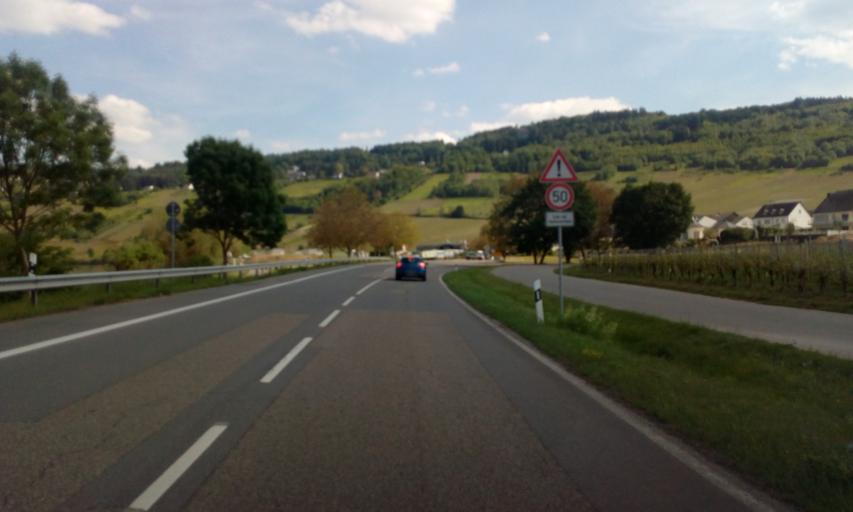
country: DE
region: Rheinland-Pfalz
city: Leiwen
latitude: 49.8197
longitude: 6.8854
